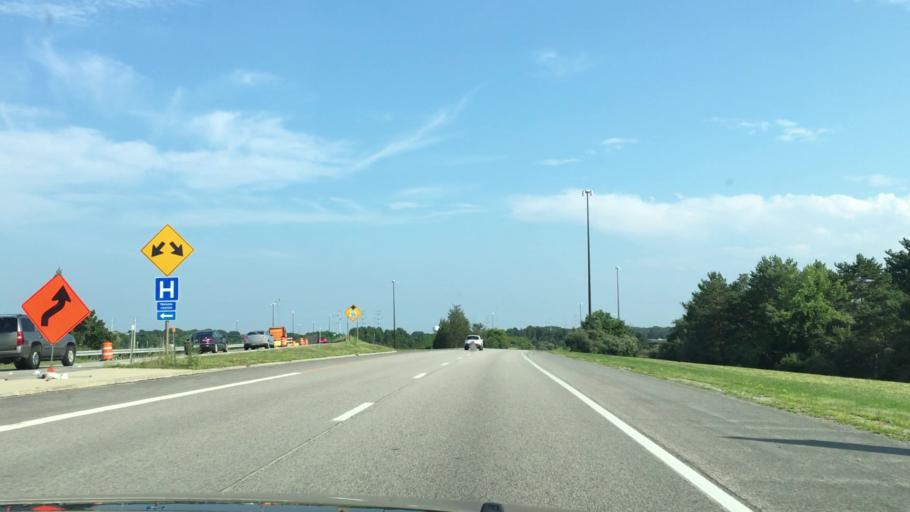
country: US
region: New Hampshire
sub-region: Rockingham County
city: Portsmouth
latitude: 43.0803
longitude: -70.7910
